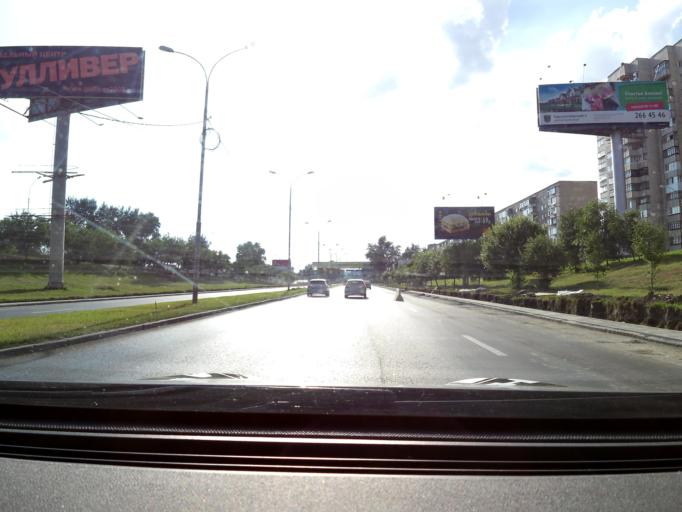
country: RU
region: Sverdlovsk
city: Sovkhoznyy
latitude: 56.8264
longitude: 60.5435
